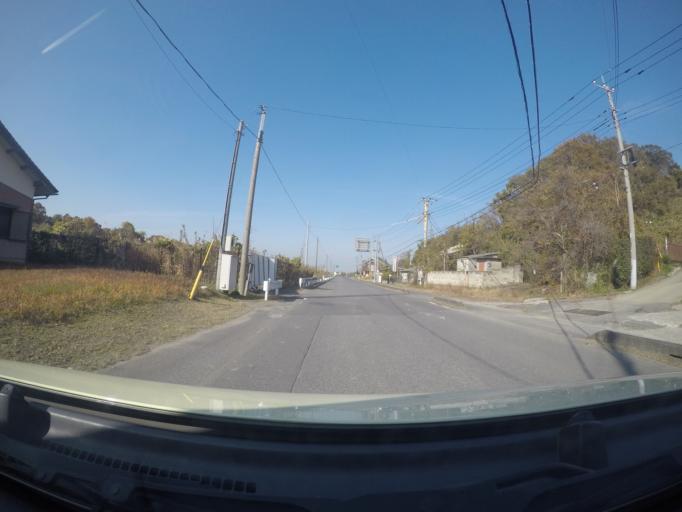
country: JP
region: Ibaraki
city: Tsukuba
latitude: 36.1857
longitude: 140.0936
